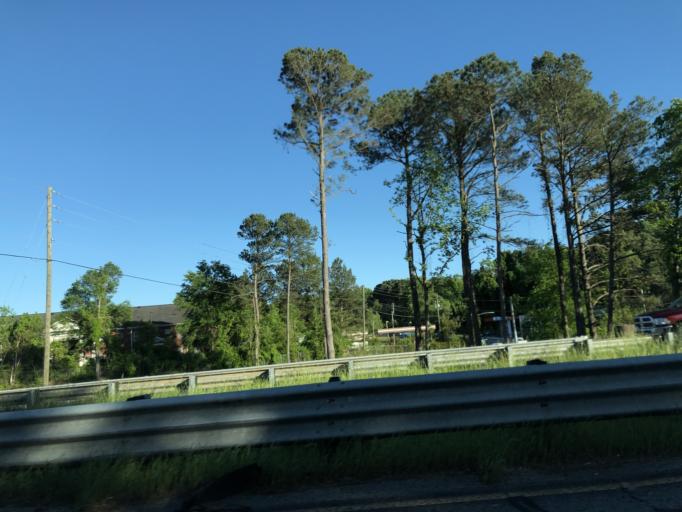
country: US
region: Georgia
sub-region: Clarke County
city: Country Club Estates
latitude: 33.9645
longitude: -83.4279
